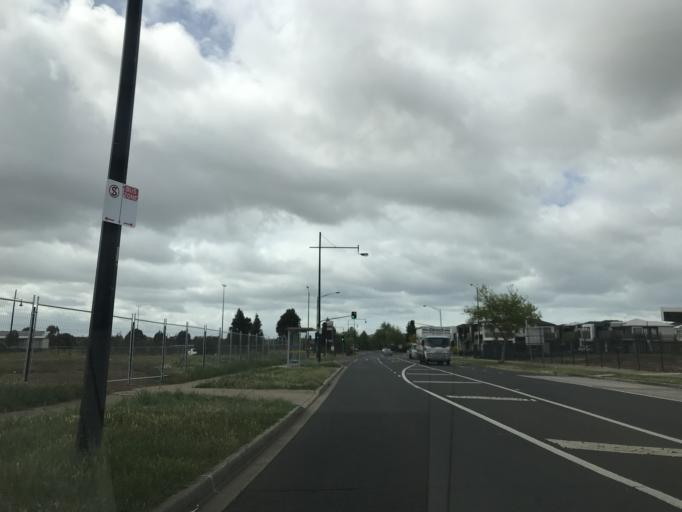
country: AU
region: Victoria
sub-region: Brimbank
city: Derrimut
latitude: -37.7908
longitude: 144.7615
